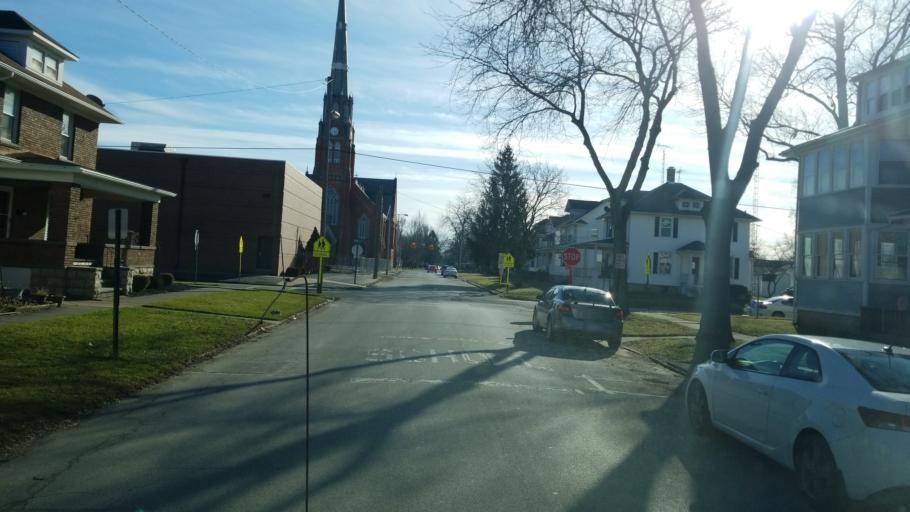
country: US
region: Ohio
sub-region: Sandusky County
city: Fremont
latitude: 41.3479
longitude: -83.1197
